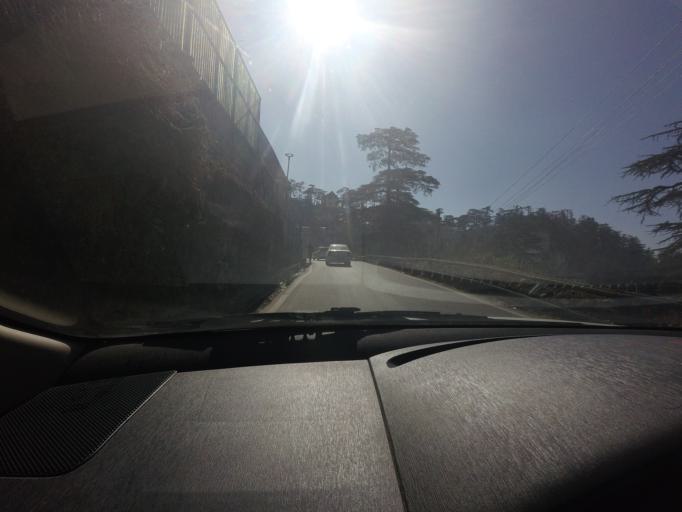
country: IN
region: Himachal Pradesh
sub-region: Shimla
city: Shimla
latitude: 31.1076
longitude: 77.1653
